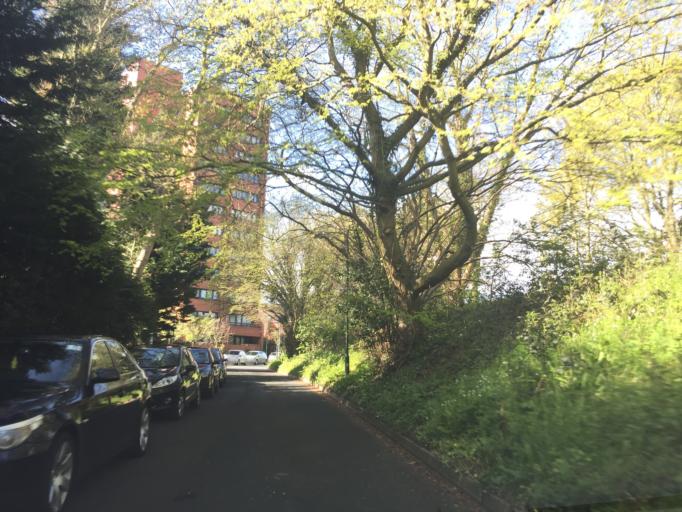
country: GB
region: England
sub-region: Essex
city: Harlow
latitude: 51.7744
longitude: 0.0970
